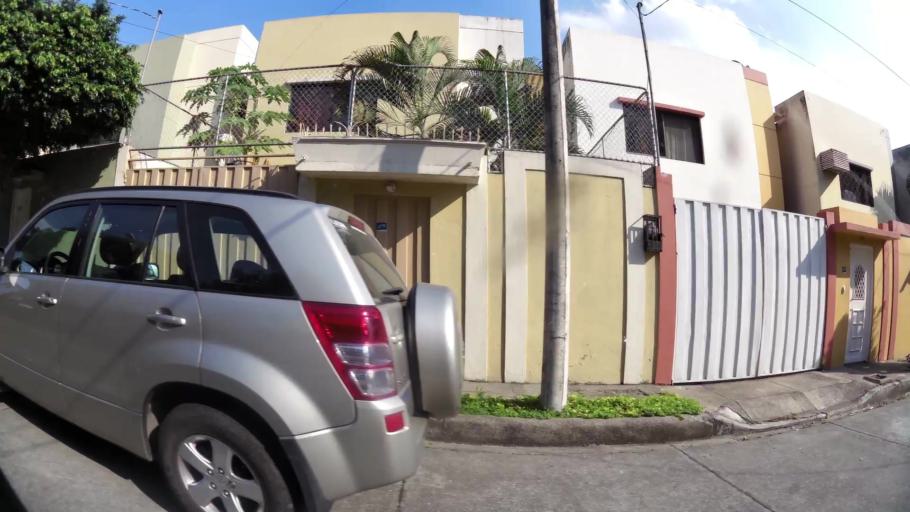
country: EC
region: Guayas
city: Guayaquil
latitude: -2.1379
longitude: -79.9264
